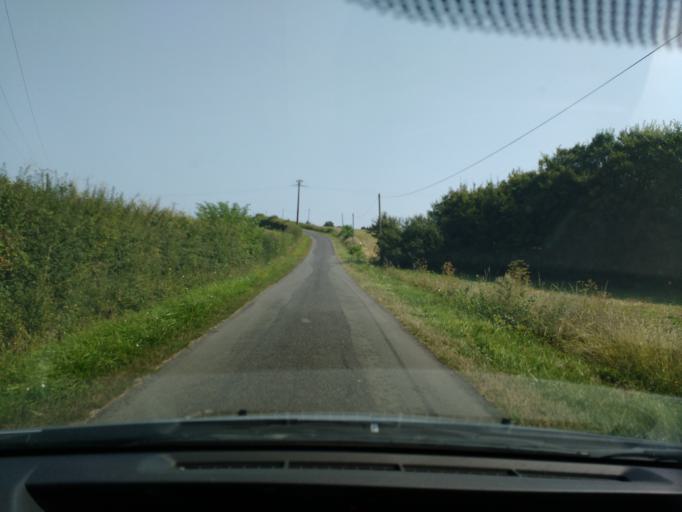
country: FR
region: Pays de la Loire
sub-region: Departement de Maine-et-Loire
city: Bauge-en-Anjou
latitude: 47.5505
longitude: -0.0376
